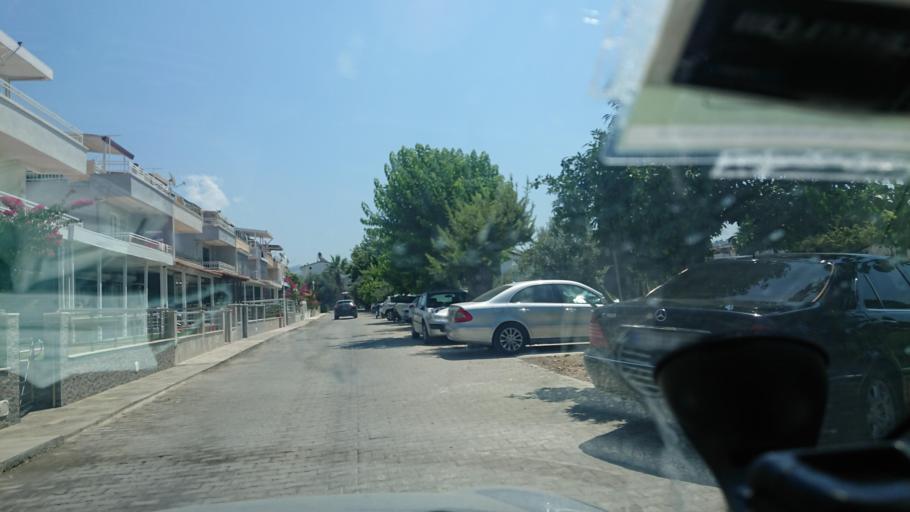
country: TR
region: Aydin
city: Kusadasi
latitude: 37.7982
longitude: 27.2727
